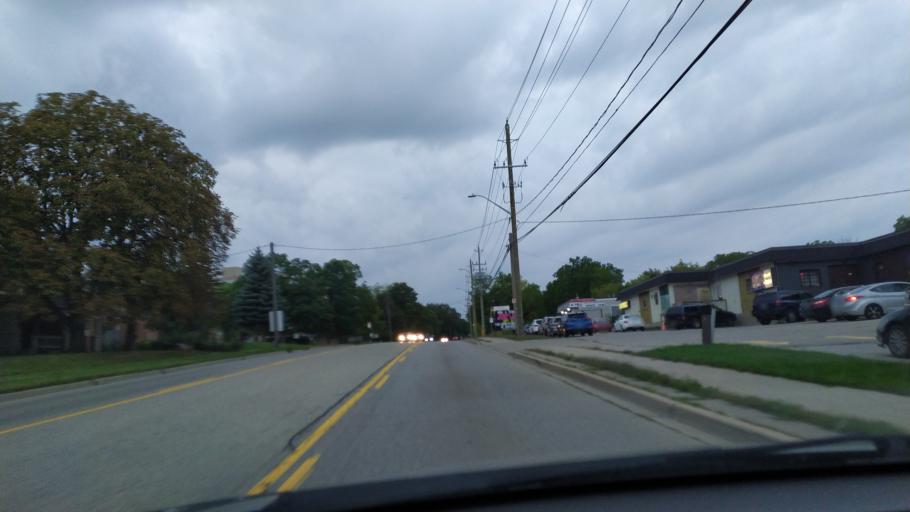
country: CA
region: Ontario
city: Kitchener
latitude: 43.4255
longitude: -80.4218
